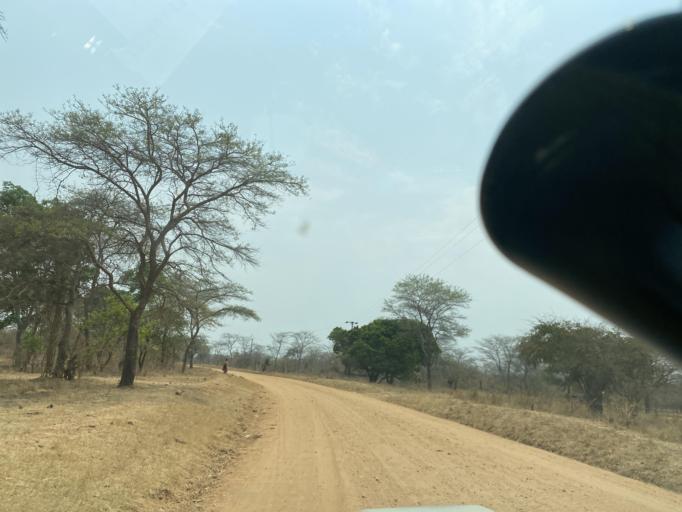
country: ZM
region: Lusaka
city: Kafue
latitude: -15.6118
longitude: 28.1081
